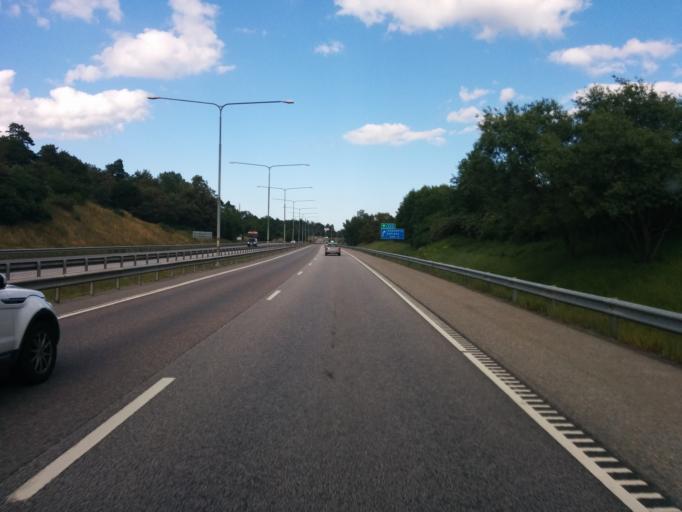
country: SE
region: Stockholm
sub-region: Nacka Kommun
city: Fisksatra
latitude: 59.3143
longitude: 18.2421
